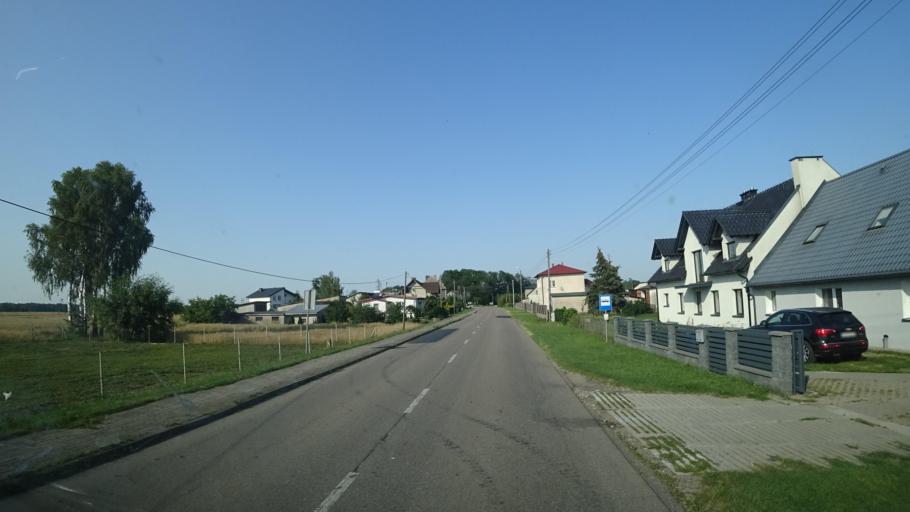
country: PL
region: Pomeranian Voivodeship
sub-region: Powiat czluchowski
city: Przechlewo
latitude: 53.8198
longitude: 17.3682
